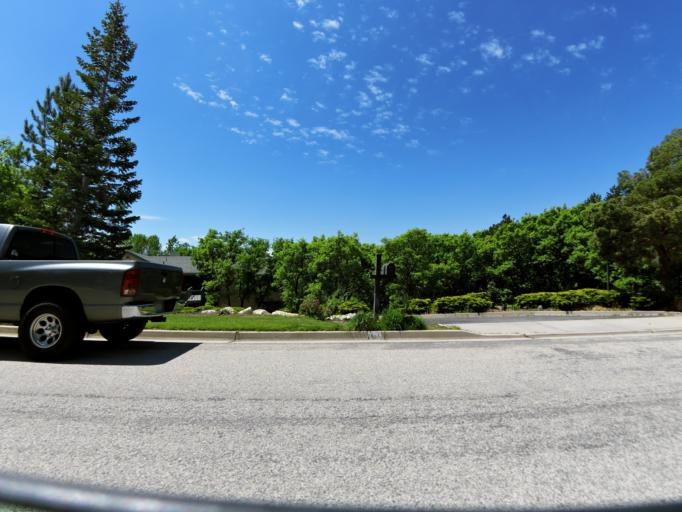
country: US
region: Utah
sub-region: Weber County
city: Uintah
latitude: 41.1585
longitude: -111.9181
